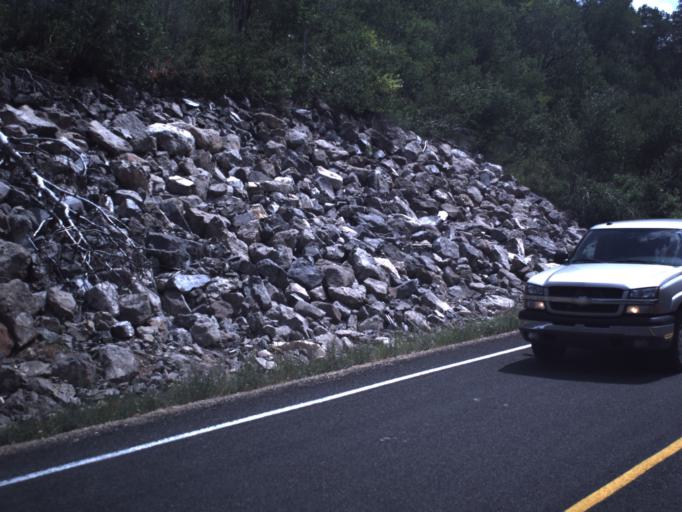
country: US
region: Utah
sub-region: Summit County
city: Francis
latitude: 40.5302
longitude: -111.0961
